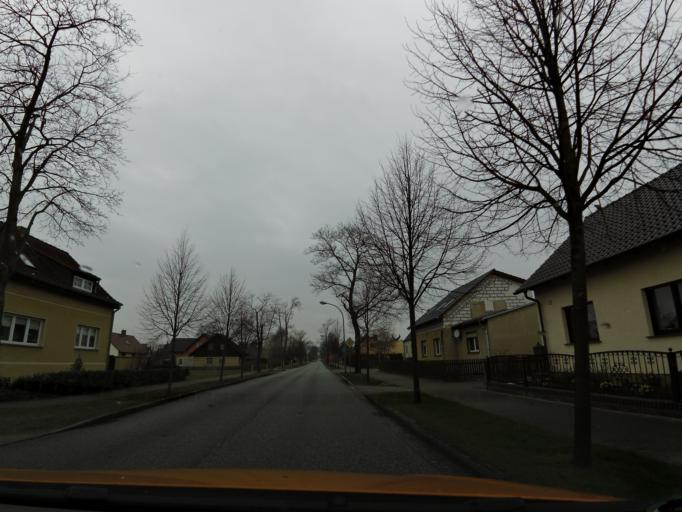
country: DE
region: Brandenburg
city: Gross Kreutz
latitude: 52.4014
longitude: 12.7931
